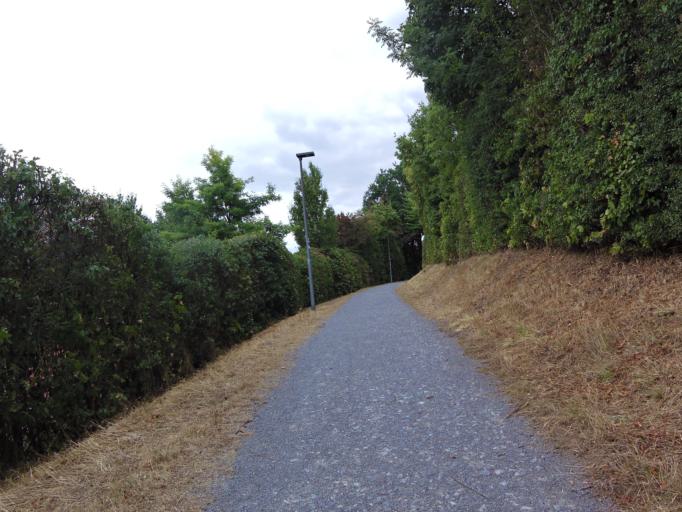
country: DE
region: Bavaria
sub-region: Regierungsbezirk Unterfranken
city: Veitshochheim
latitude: 49.8317
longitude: 9.8844
